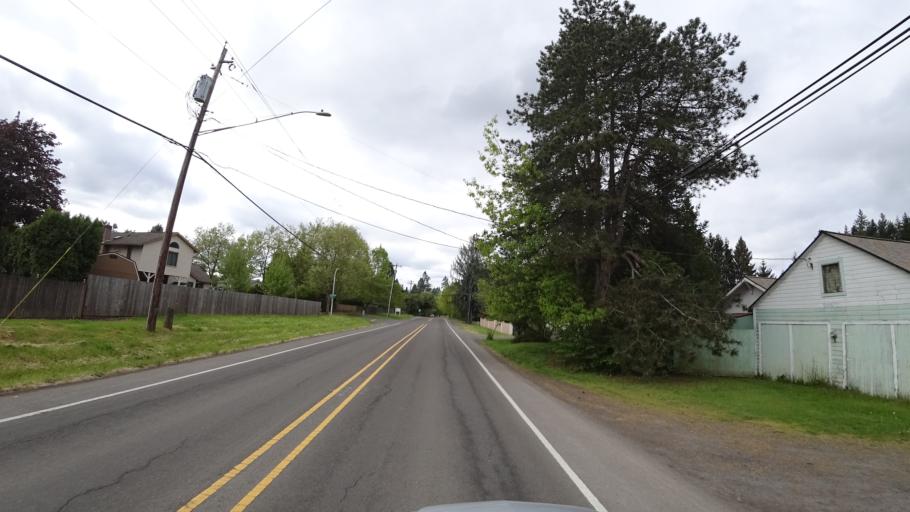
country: US
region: Oregon
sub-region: Washington County
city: Hillsboro
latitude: 45.5345
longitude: -122.9797
